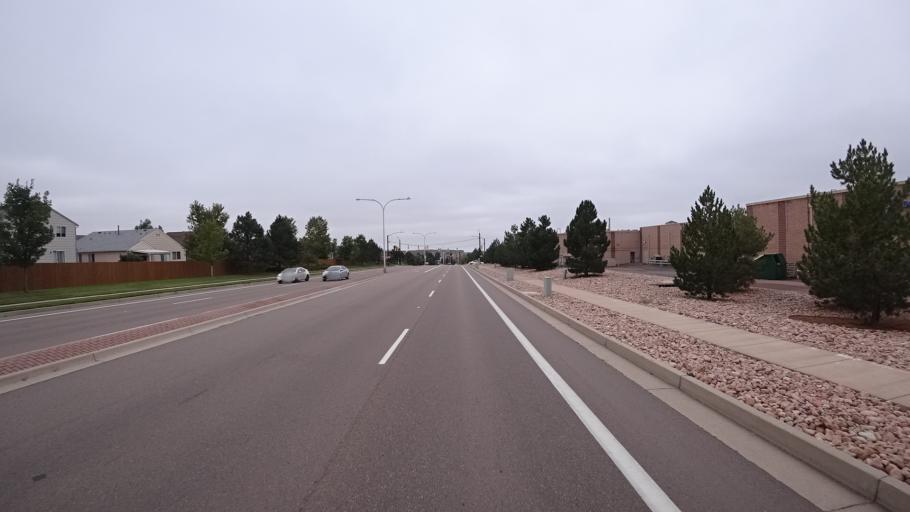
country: US
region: Colorado
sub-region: El Paso County
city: Cimarron Hills
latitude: 38.9142
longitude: -104.7164
